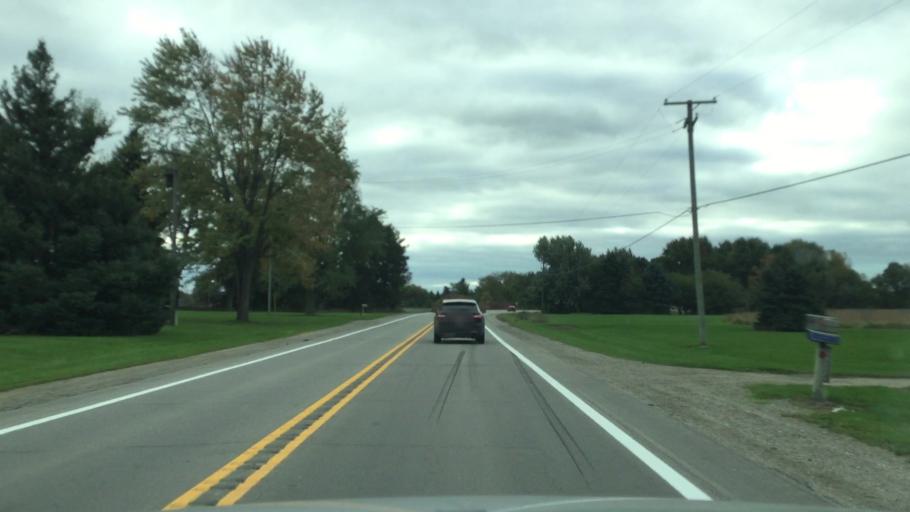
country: US
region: Michigan
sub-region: Macomb County
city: Memphis
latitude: 42.8567
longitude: -82.7651
